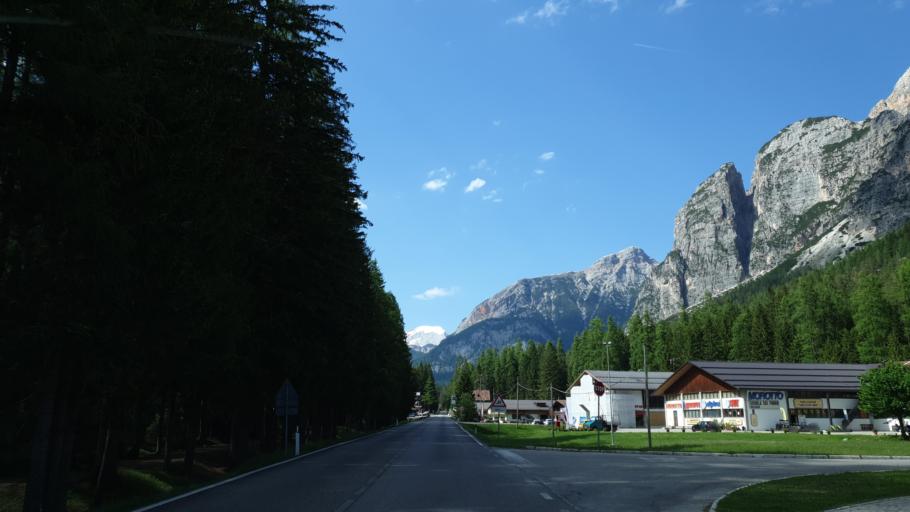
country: IT
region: Veneto
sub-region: Provincia di Belluno
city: Cortina d'Ampezzo
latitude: 46.5731
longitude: 12.1173
